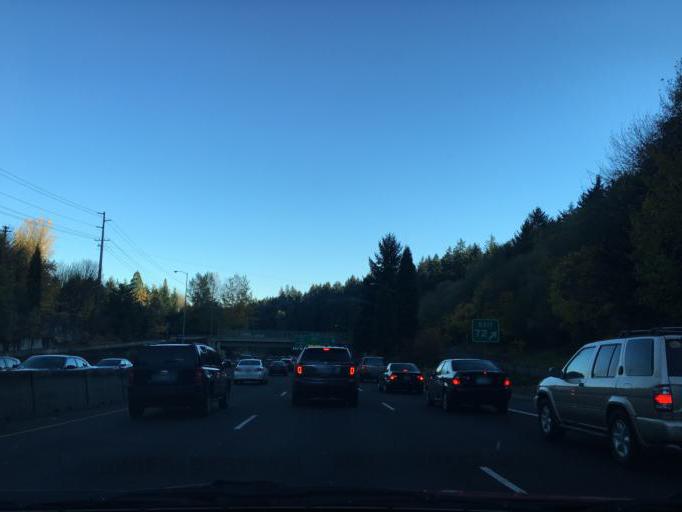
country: US
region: Oregon
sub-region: Washington County
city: West Slope
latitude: 45.5077
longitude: -122.7213
